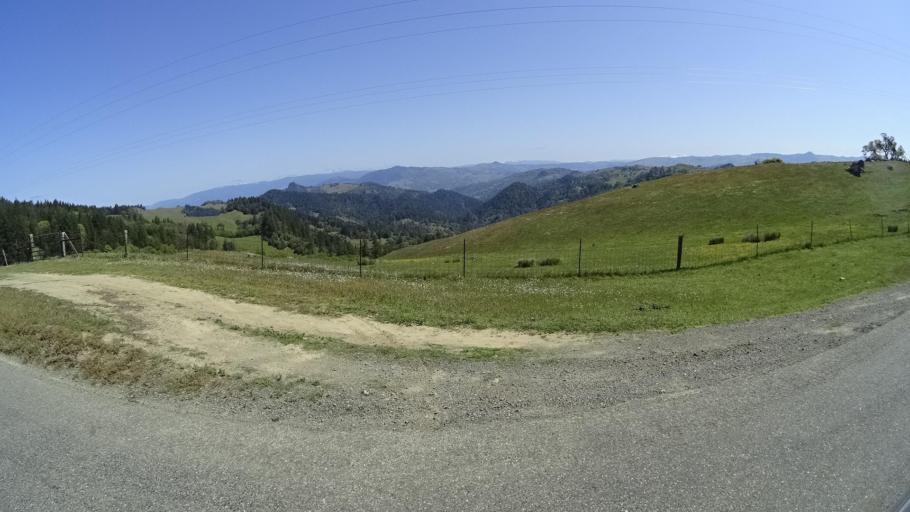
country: US
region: California
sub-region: Humboldt County
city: Redway
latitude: 40.0292
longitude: -123.6352
